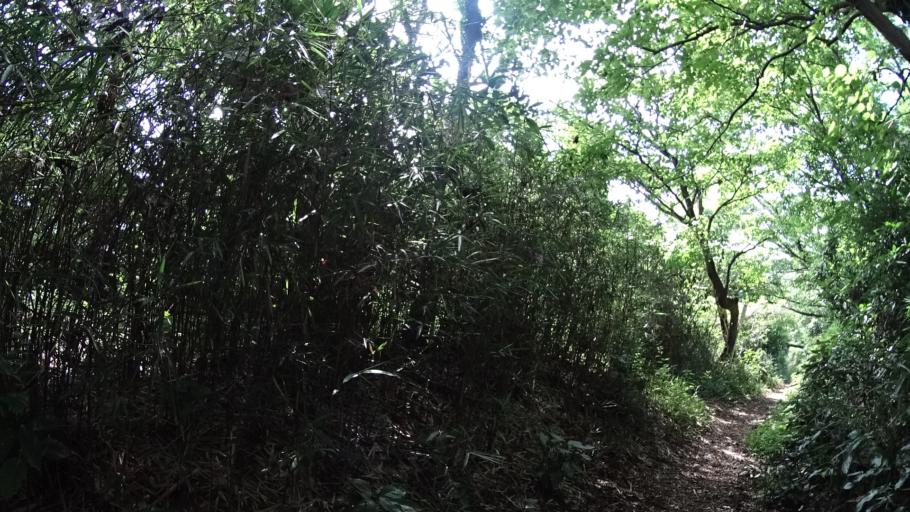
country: JP
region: Kanagawa
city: Zushi
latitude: 35.3124
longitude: 139.6102
